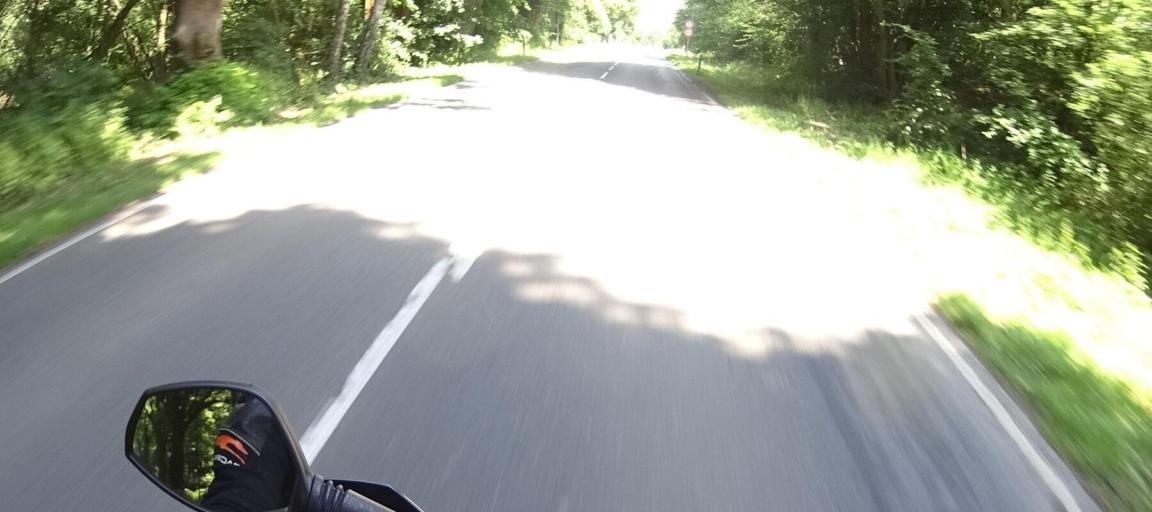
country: DE
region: North Rhine-Westphalia
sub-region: Regierungsbezirk Detmold
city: Hoexter
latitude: 51.7814
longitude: 9.4277
